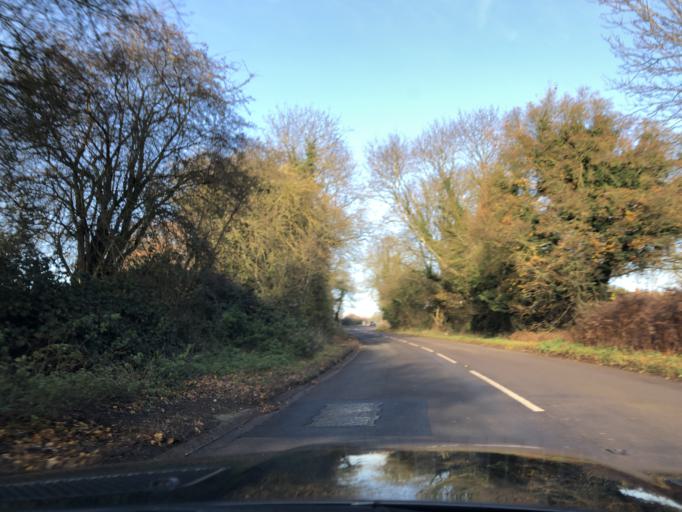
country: GB
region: England
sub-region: Buckinghamshire
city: Marlow
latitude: 51.5920
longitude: -0.7668
